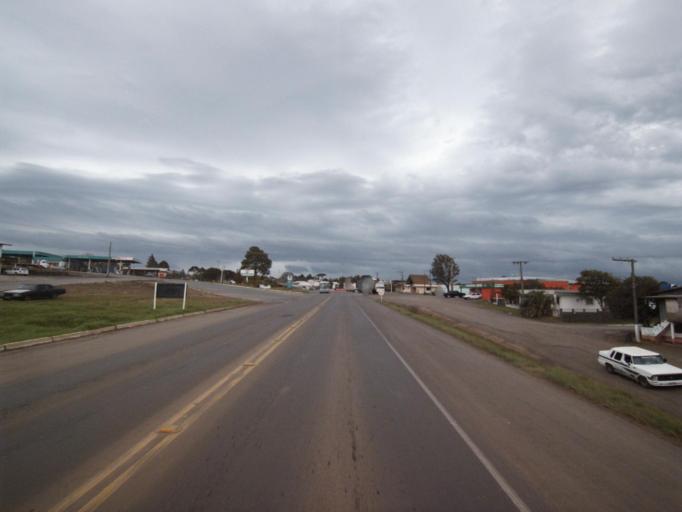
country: BR
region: Santa Catarina
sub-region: Concordia
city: Concordia
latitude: -27.0204
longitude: -51.8847
